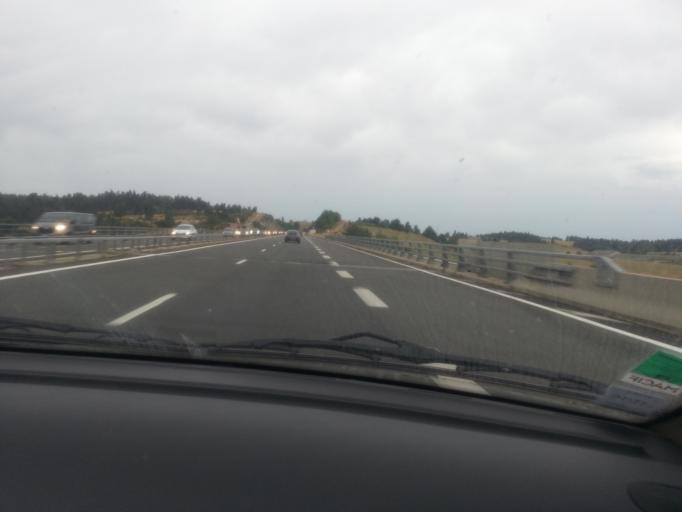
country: FR
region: Languedoc-Roussillon
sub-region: Departement de la Lozere
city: Aumont-Aubrac
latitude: 44.6384
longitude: 3.2417
